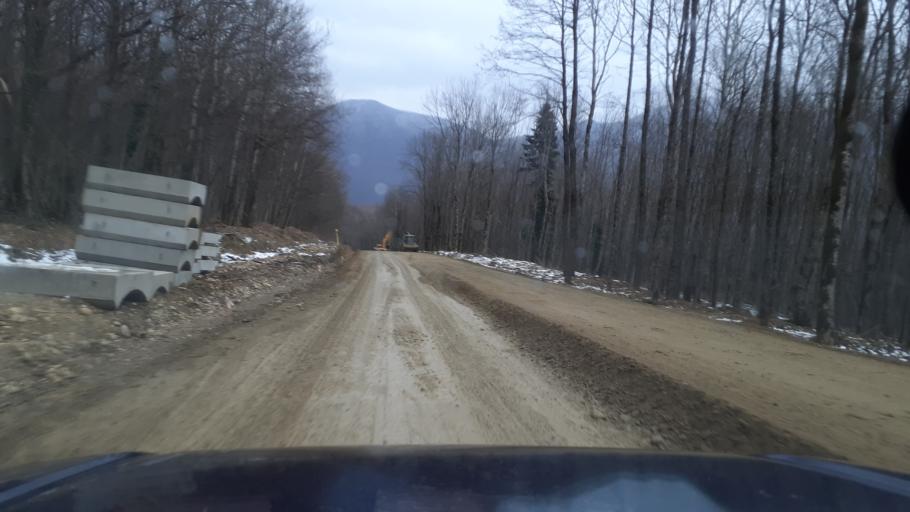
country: RU
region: Krasnodarskiy
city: Neftegorsk
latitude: 44.1639
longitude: 39.8023
